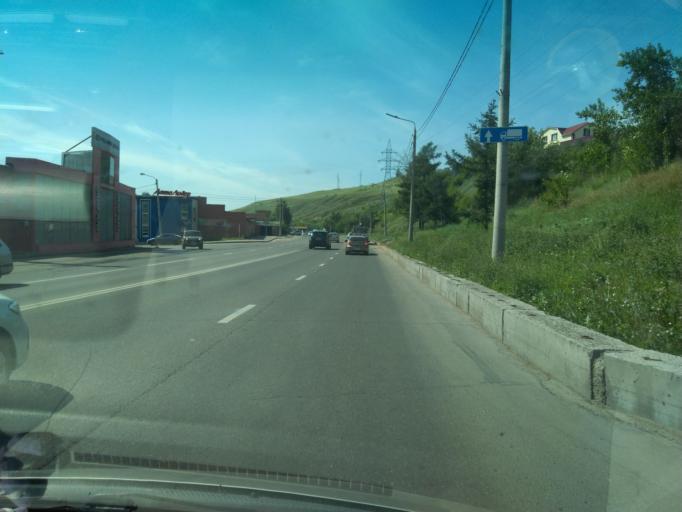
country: RU
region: Krasnoyarskiy
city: Krasnoyarsk
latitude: 56.0202
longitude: 92.8744
